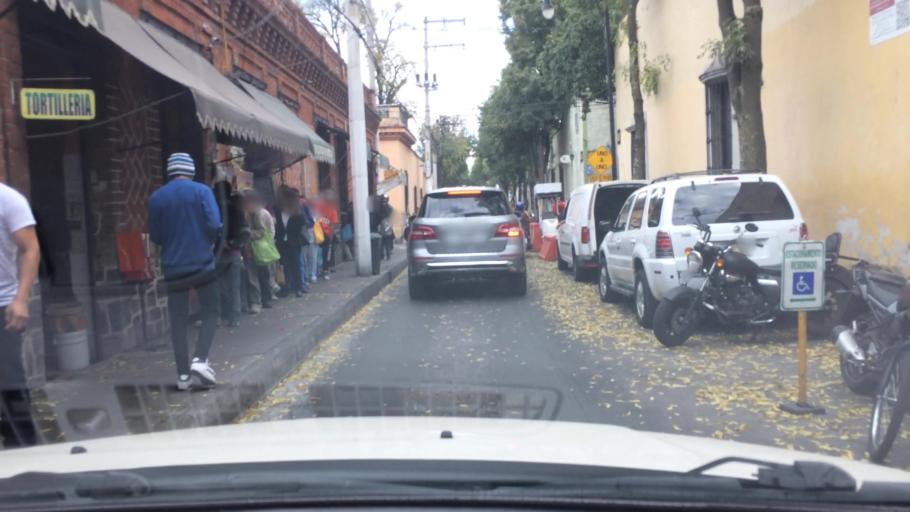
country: MX
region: Mexico City
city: Tlalpan
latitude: 19.2879
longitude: -99.1673
